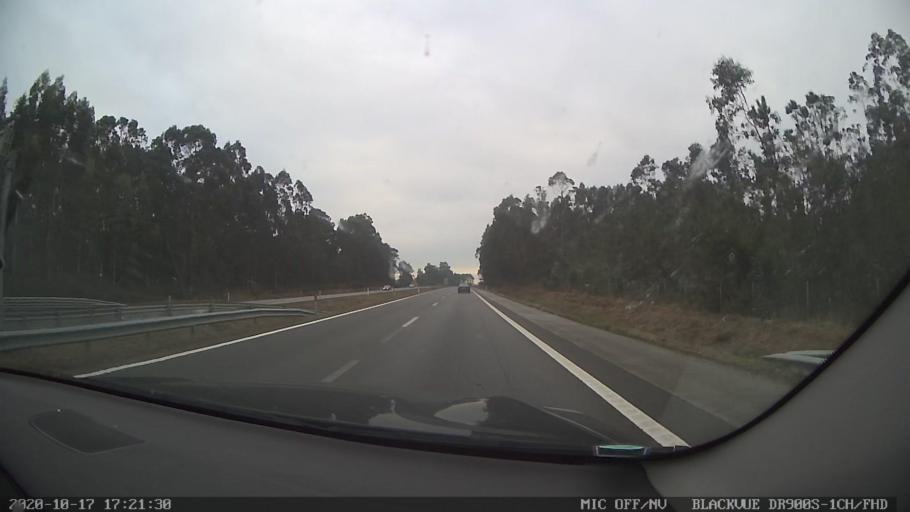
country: PT
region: Porto
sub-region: Povoa de Varzim
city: Pedroso
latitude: 41.4305
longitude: -8.7450
